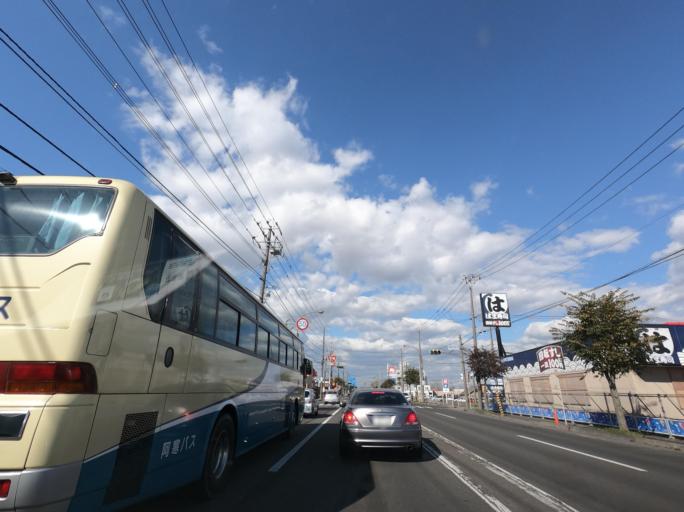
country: JP
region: Hokkaido
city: Kushiro
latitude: 43.0110
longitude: 144.3592
